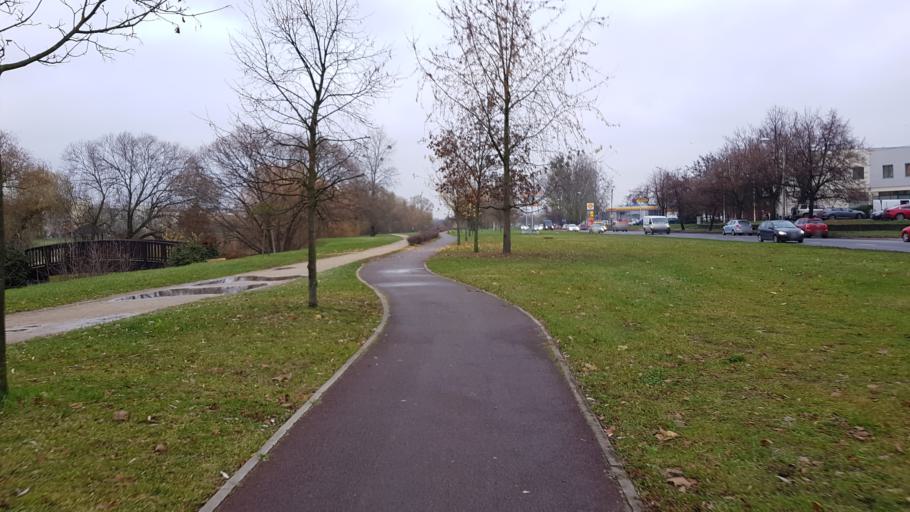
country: PL
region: West Pomeranian Voivodeship
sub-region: Szczecin
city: Szczecin
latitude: 53.4231
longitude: 14.5002
